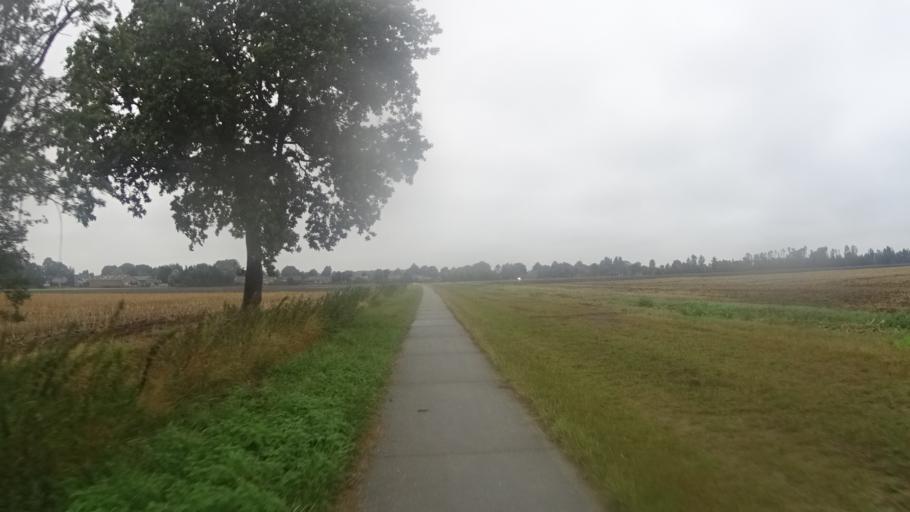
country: NL
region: Groningen
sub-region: Gemeente Slochteren
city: Slochteren
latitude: 53.1885
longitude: 6.8785
